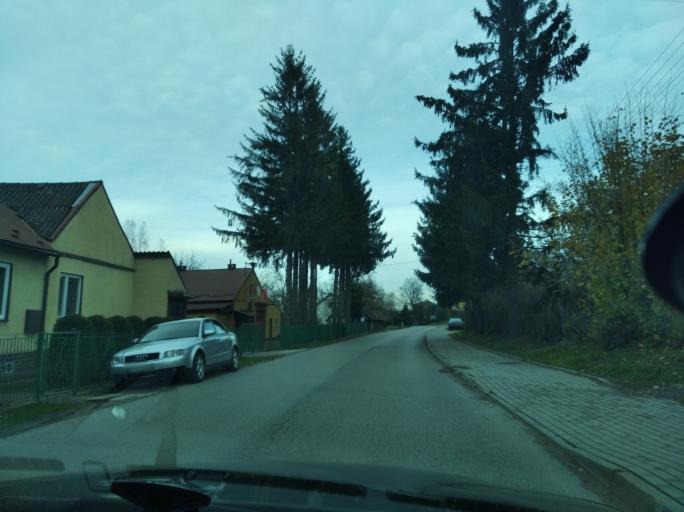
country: PL
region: Subcarpathian Voivodeship
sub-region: Powiat przeworski
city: Grzeska
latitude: 50.0761
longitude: 22.4532
